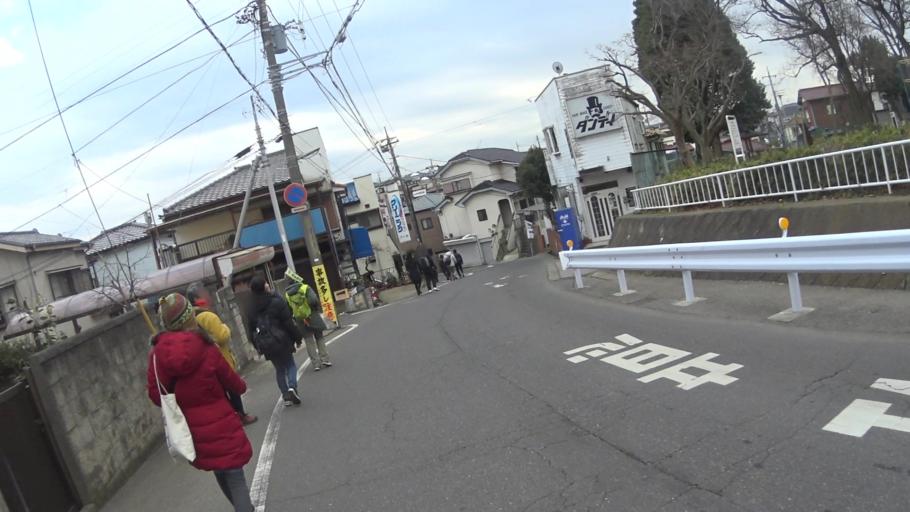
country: JP
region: Chiba
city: Funabashi
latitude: 35.7489
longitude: 139.9916
